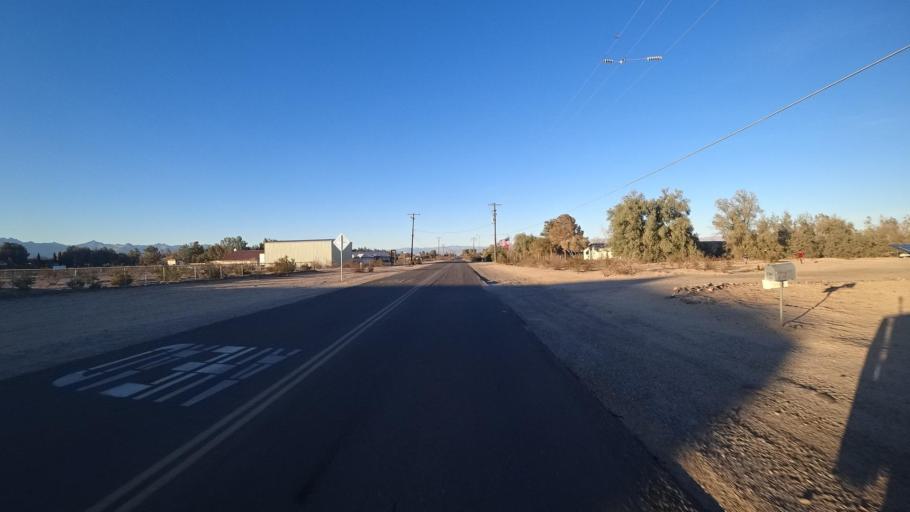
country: US
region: California
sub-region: Kern County
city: Ridgecrest
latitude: 35.6310
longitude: -117.7054
